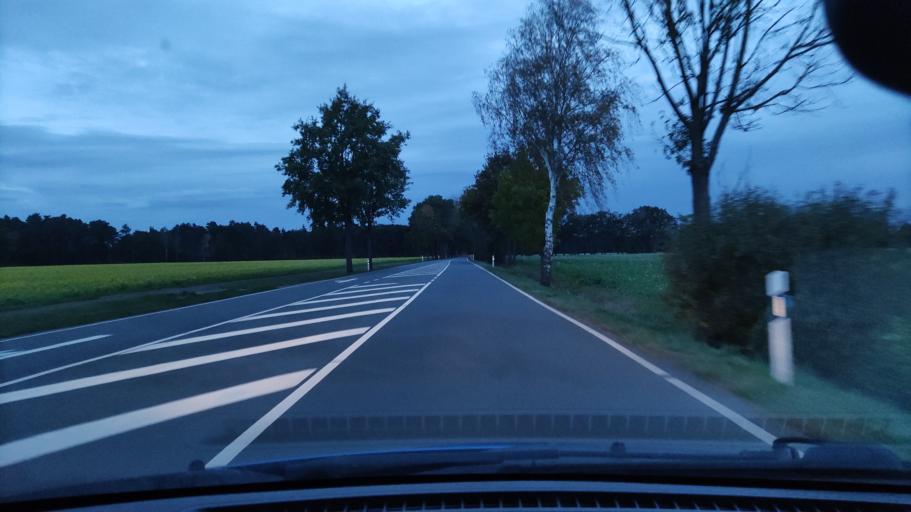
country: DE
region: Lower Saxony
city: Trebel
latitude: 52.9707
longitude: 11.2768
